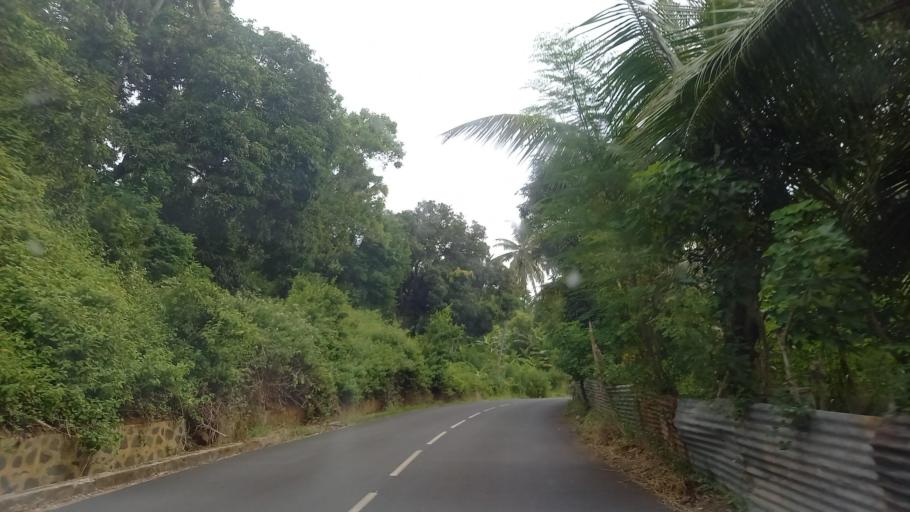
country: YT
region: Boueni
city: Boueni
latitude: -12.9024
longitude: 45.0888
